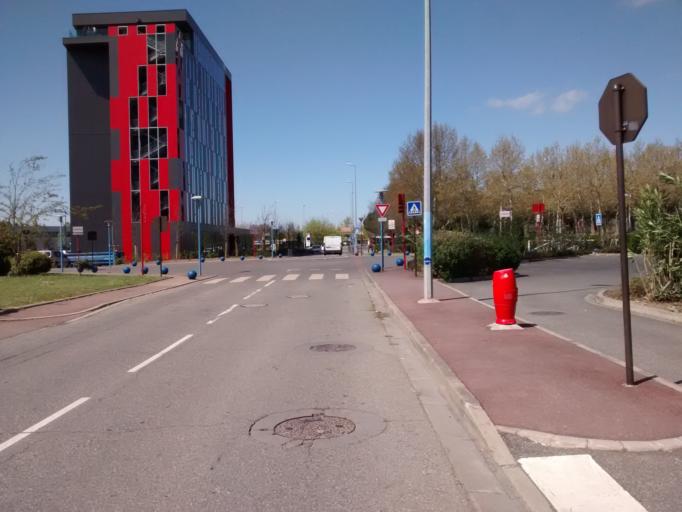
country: FR
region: Midi-Pyrenees
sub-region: Departement de la Haute-Garonne
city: Saint-Orens-de-Gameville
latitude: 43.5411
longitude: 1.5133
